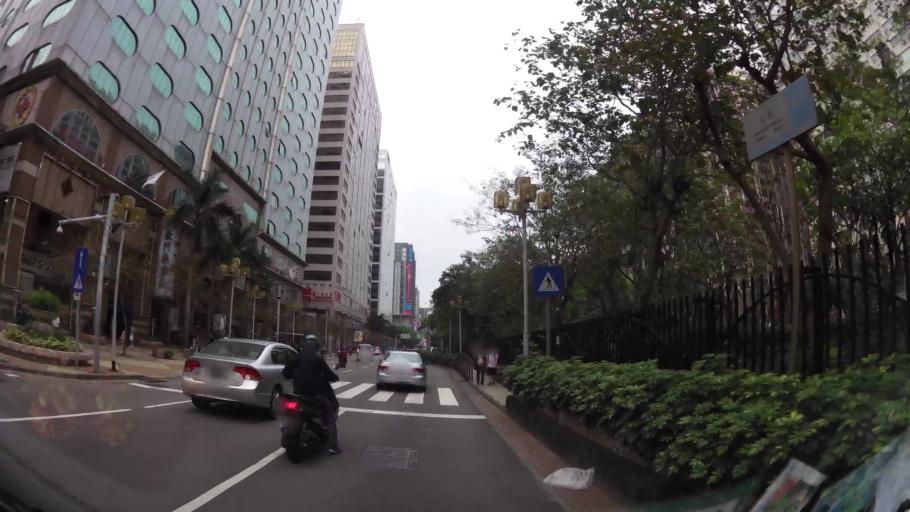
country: MO
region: Macau
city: Macau
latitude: 22.1885
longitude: 113.5506
